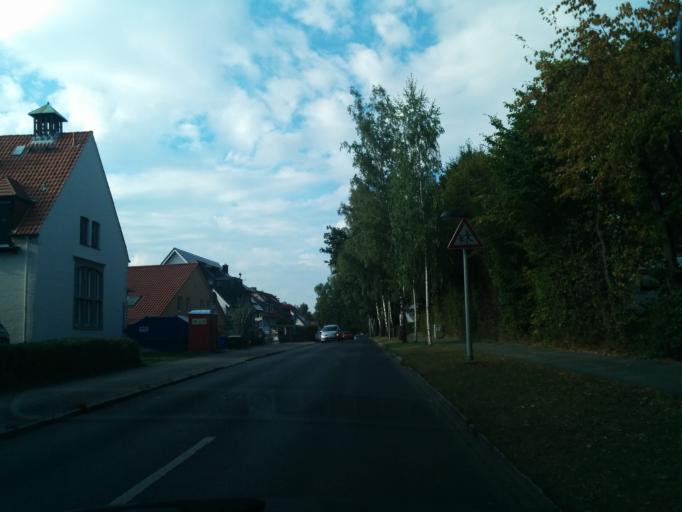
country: DE
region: Lower Saxony
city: Goettingen
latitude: 51.5278
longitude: 9.9541
